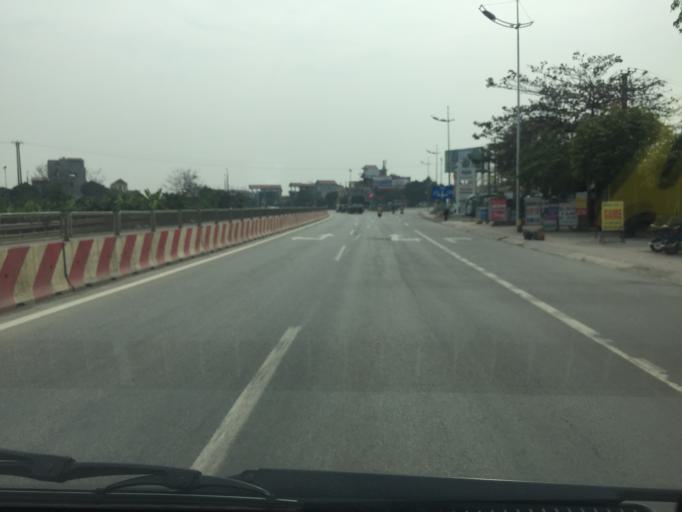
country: VN
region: Ninh Binh
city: Thanh Pho Ninh Binh
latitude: 20.2197
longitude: 105.9649
